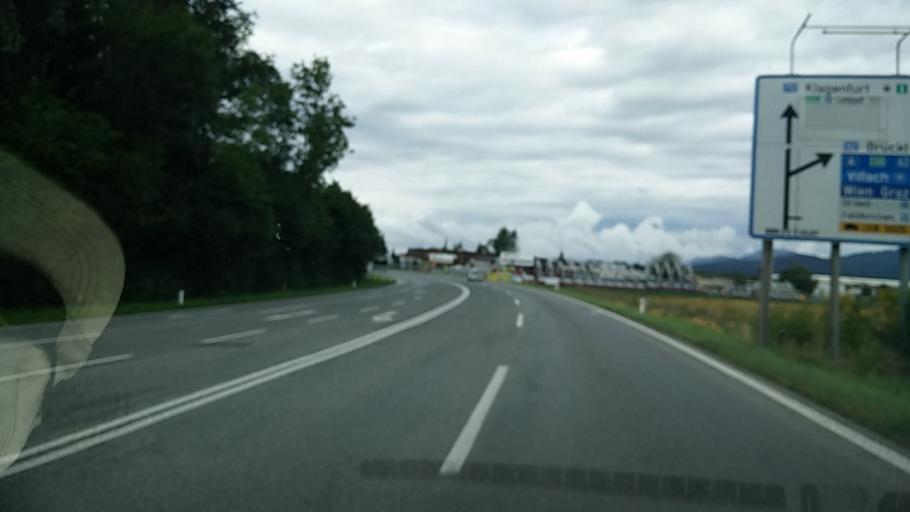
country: AT
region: Carinthia
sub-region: Politischer Bezirk Klagenfurt Land
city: Ebenthal
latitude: 46.6284
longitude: 14.3751
